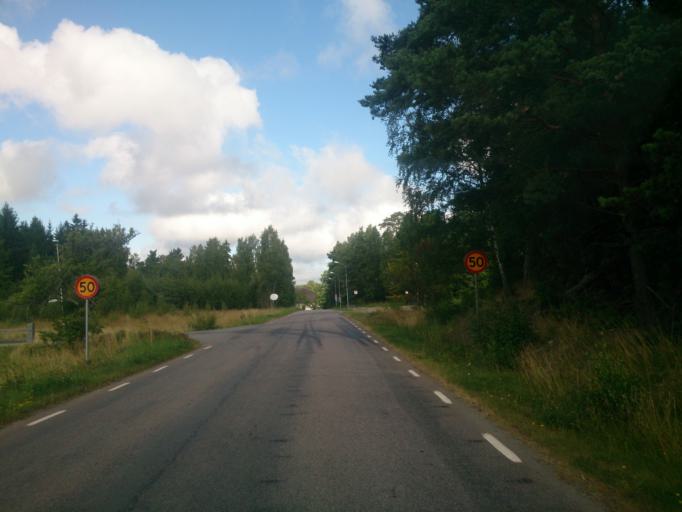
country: SE
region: OEstergoetland
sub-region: Linkopings Kommun
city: Sturefors
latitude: 58.2966
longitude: 15.8690
